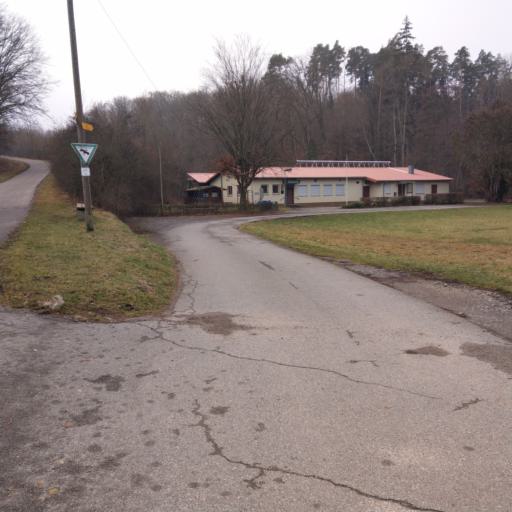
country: DE
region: Baden-Wuerttemberg
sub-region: Regierungsbezirk Stuttgart
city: Waldenbuch
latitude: 48.6319
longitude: 9.1199
